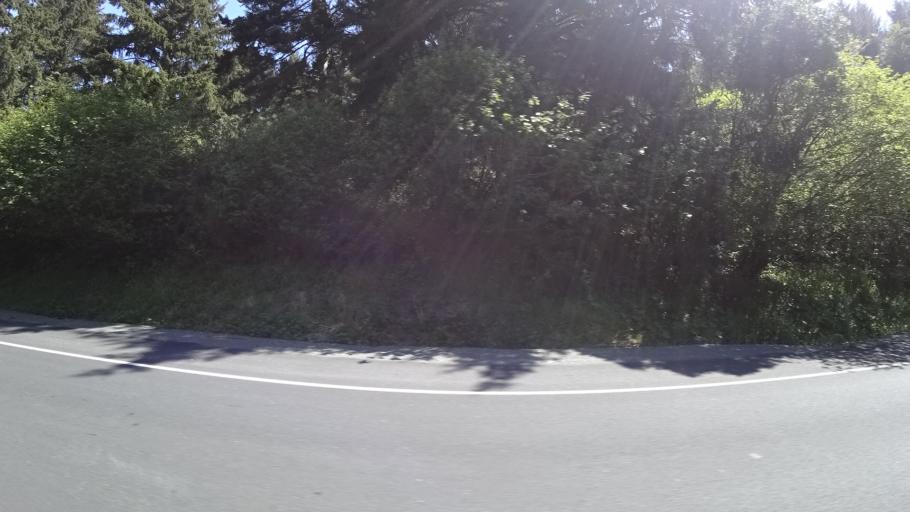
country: US
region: California
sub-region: Humboldt County
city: Westhaven-Moonstone
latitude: 41.2019
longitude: -124.1108
